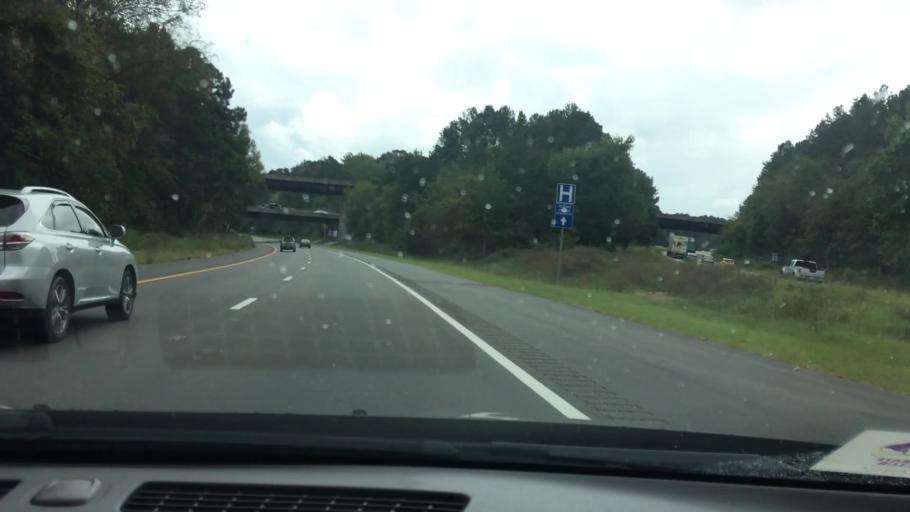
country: US
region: North Carolina
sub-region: Wake County
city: Raleigh
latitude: 35.7544
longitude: -78.5980
